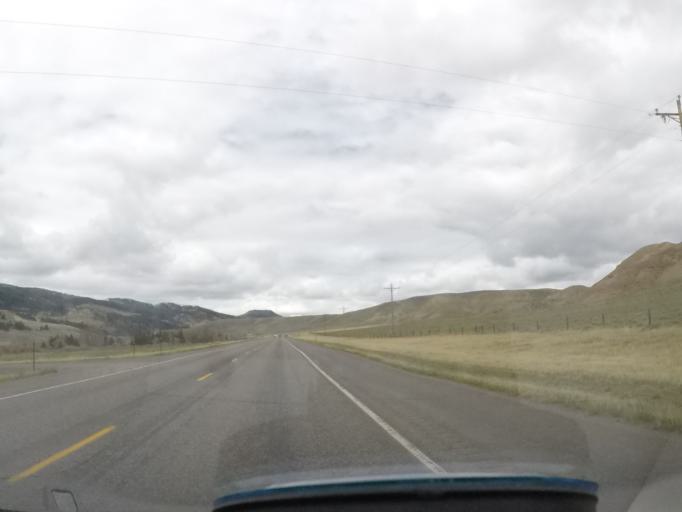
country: US
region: Wyoming
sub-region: Sublette County
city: Pinedale
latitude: 43.5745
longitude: -109.7299
